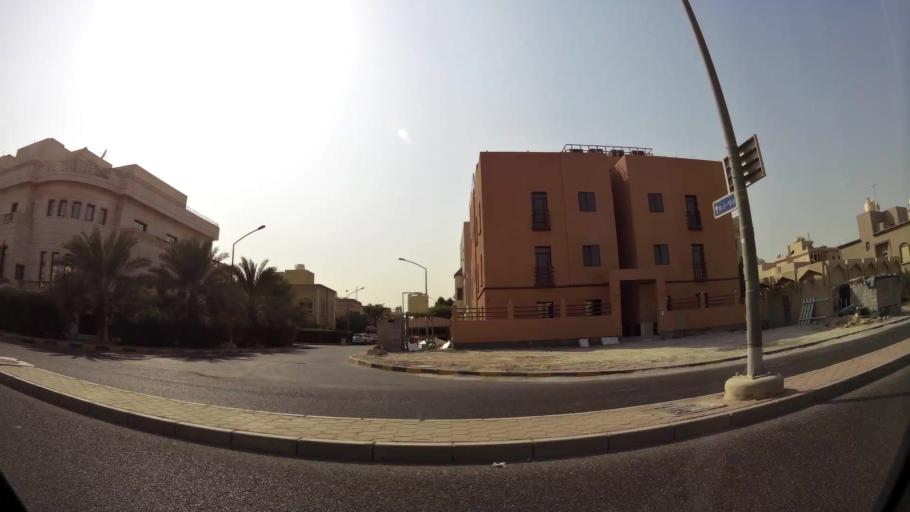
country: KW
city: Bayan
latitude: 29.2855
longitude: 48.0482
